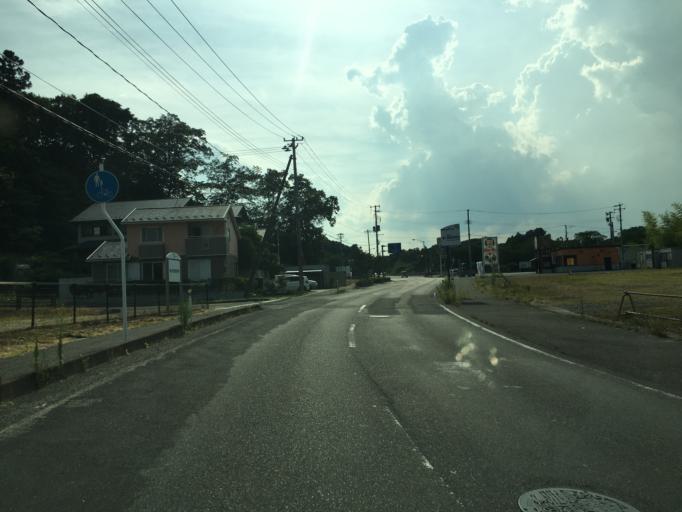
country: JP
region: Fukushima
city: Miharu
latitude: 37.4470
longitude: 140.4294
